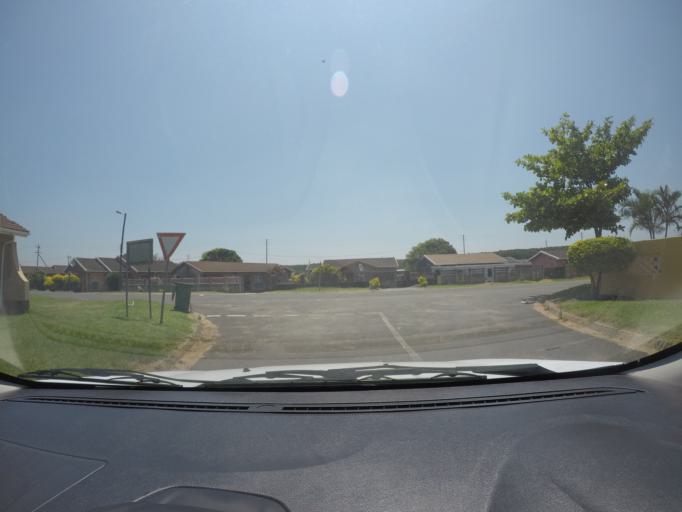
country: ZA
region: KwaZulu-Natal
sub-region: uThungulu District Municipality
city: eSikhawini
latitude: -28.8905
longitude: 31.8822
